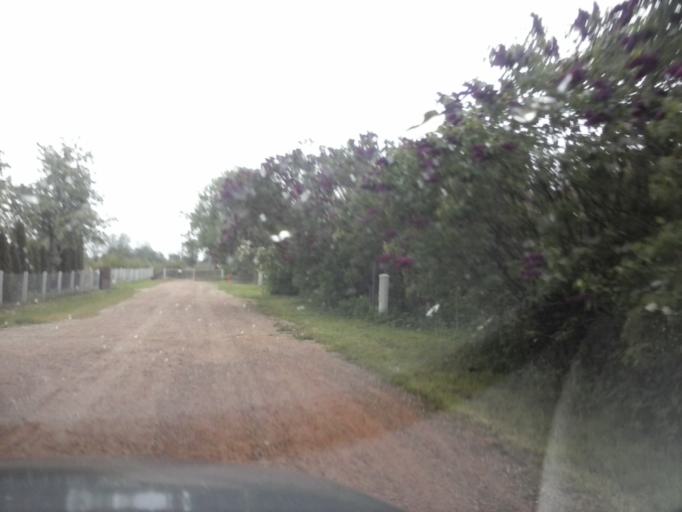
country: LV
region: Valmieras Rajons
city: Valmiera
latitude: 57.5537
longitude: 25.4375
